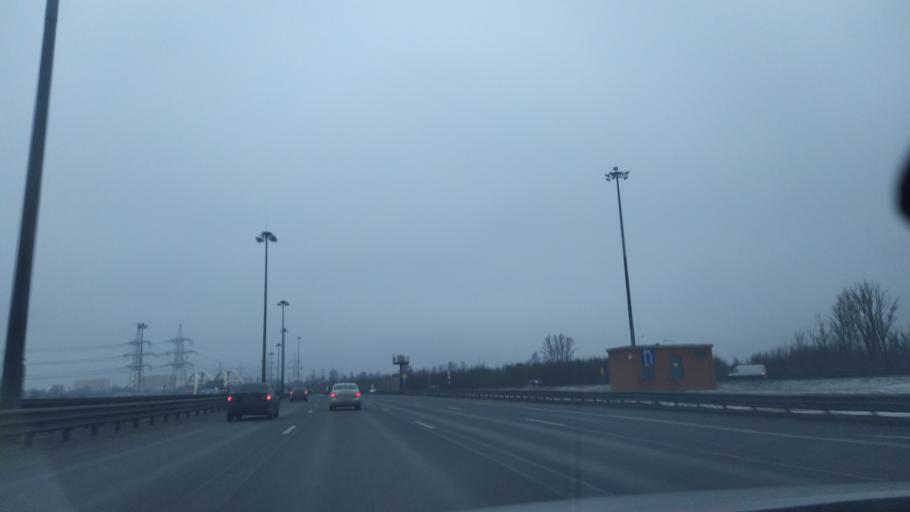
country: RU
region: St.-Petersburg
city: Krasnogvargeisky
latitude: 59.9902
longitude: 30.4832
